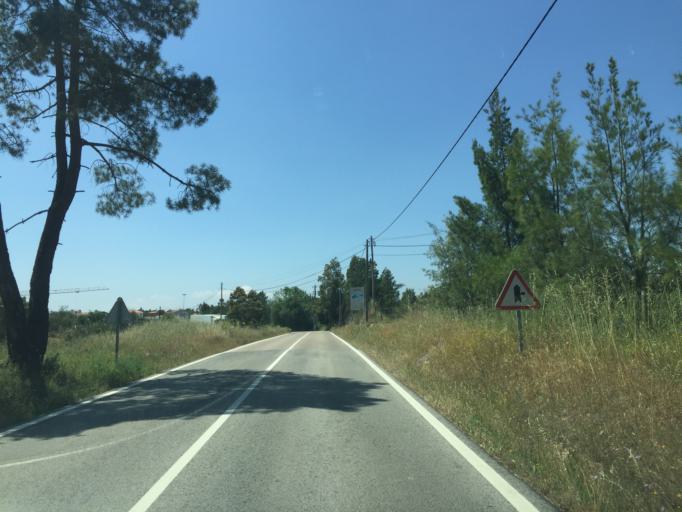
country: PT
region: Santarem
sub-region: Constancia
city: Constancia
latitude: 39.4820
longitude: -8.3234
